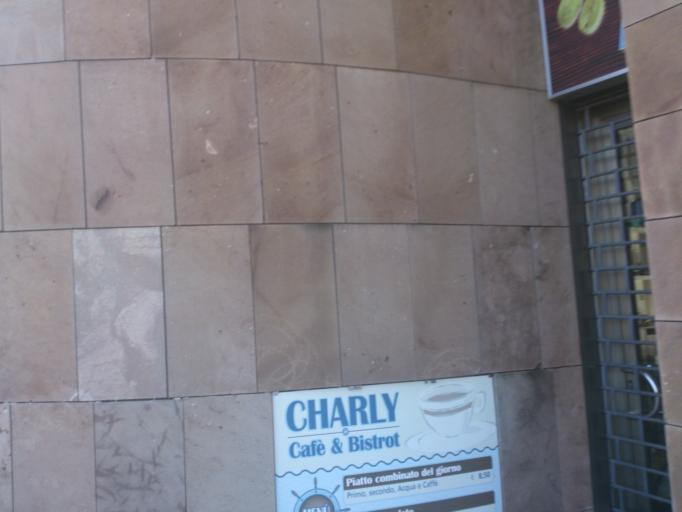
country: IT
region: Lombardy
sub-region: Citta metropolitana di Milano
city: San Donato Milanese
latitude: 45.4187
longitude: 9.2586
